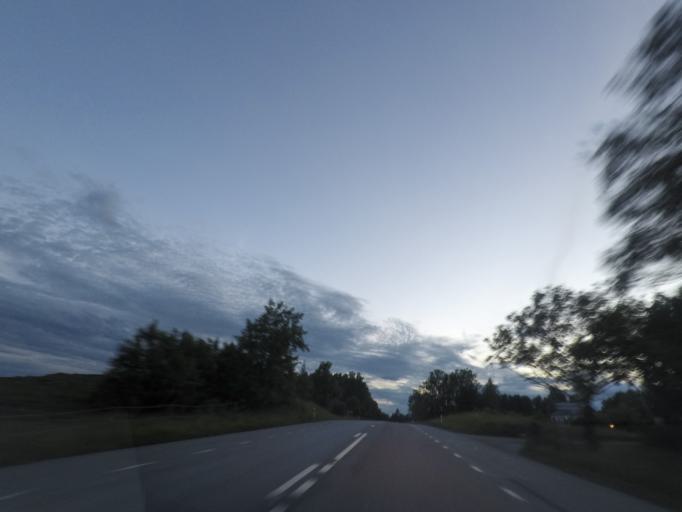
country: SE
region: Uppsala
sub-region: Enkopings Kommun
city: Orsundsbro
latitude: 59.6601
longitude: 17.3287
